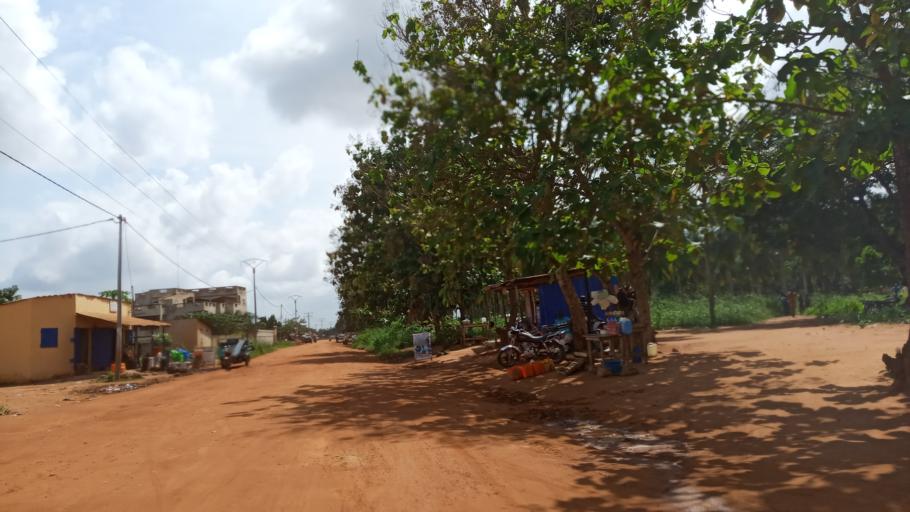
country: TG
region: Maritime
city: Lome
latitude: 6.2331
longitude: 1.1365
